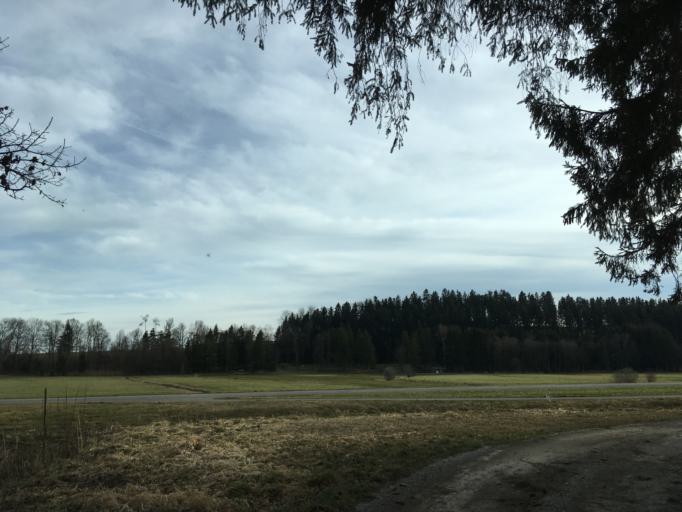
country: DE
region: Bavaria
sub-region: Upper Bavaria
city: Vogtareuth
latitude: 47.9477
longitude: 12.2068
